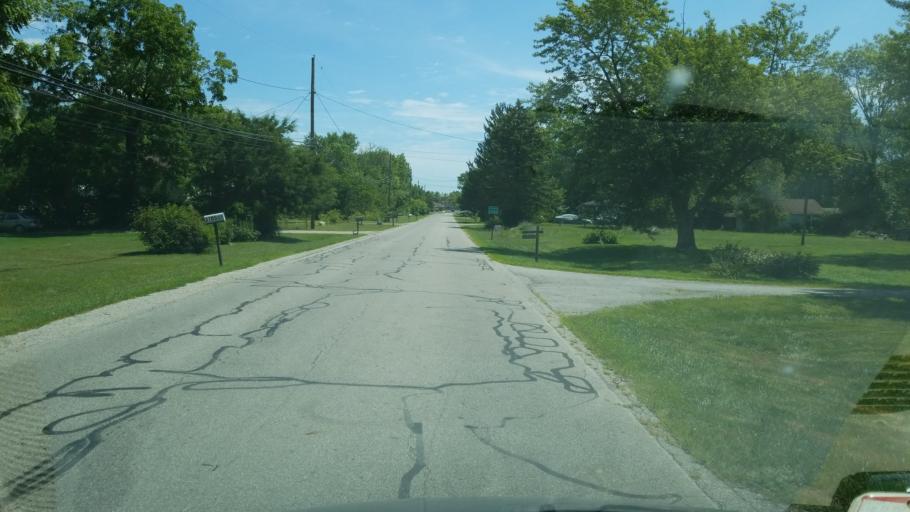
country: US
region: Ohio
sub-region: Franklin County
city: Grove City
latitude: 39.8720
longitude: -83.0895
